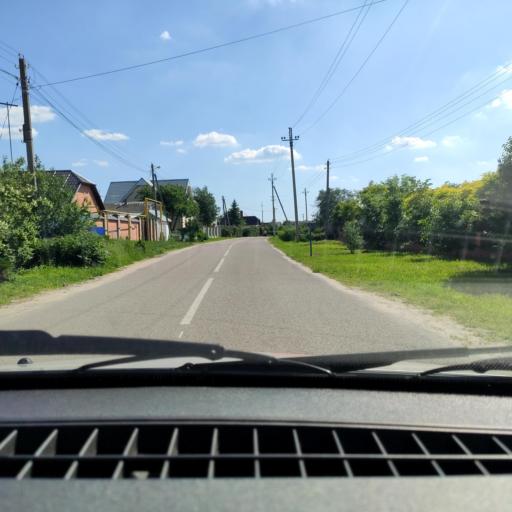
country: RU
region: Voronezj
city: Ramon'
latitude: 51.8149
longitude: 39.2639
